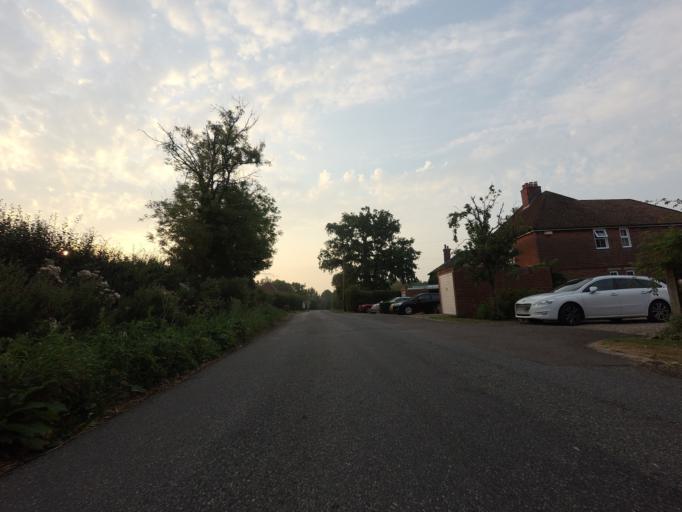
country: GB
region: England
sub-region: Kent
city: Lenham
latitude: 51.1822
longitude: 0.7210
